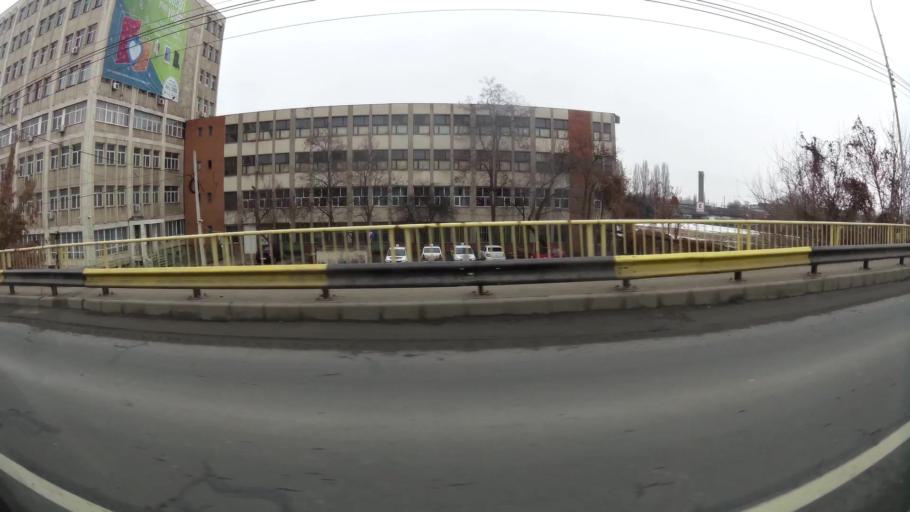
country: RO
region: Prahova
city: Ploiesti
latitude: 44.9277
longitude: 26.0330
